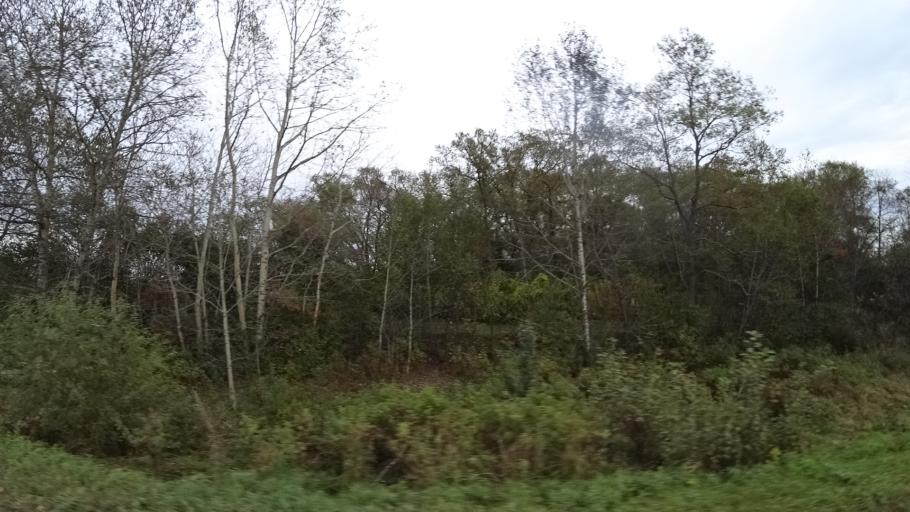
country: RU
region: Amur
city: Arkhara
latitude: 49.4353
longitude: 130.2556
